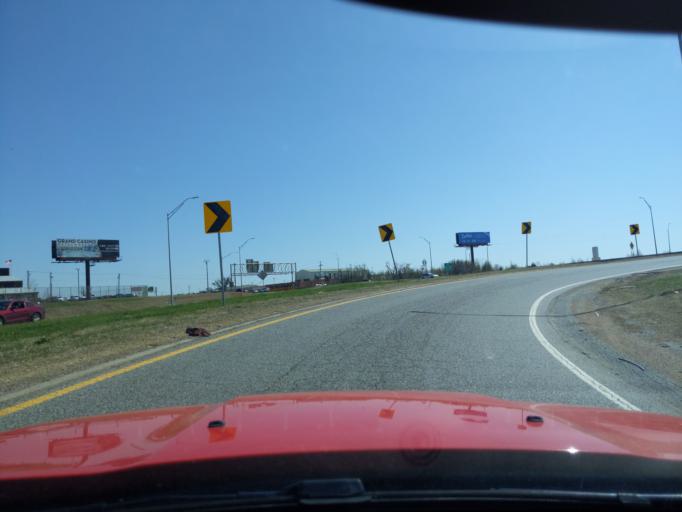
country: US
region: Oklahoma
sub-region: Cleveland County
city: Moore
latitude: 35.3925
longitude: -97.4939
